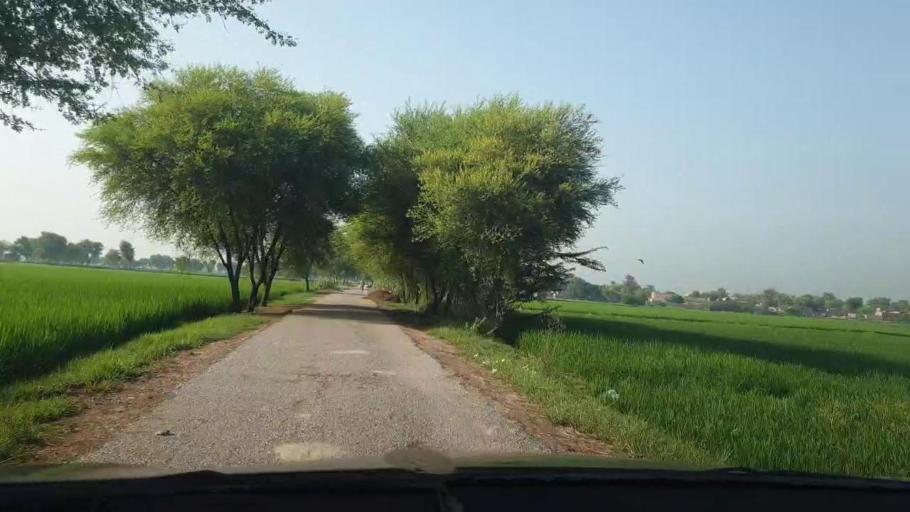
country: PK
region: Sindh
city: Kambar
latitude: 27.5747
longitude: 68.1026
